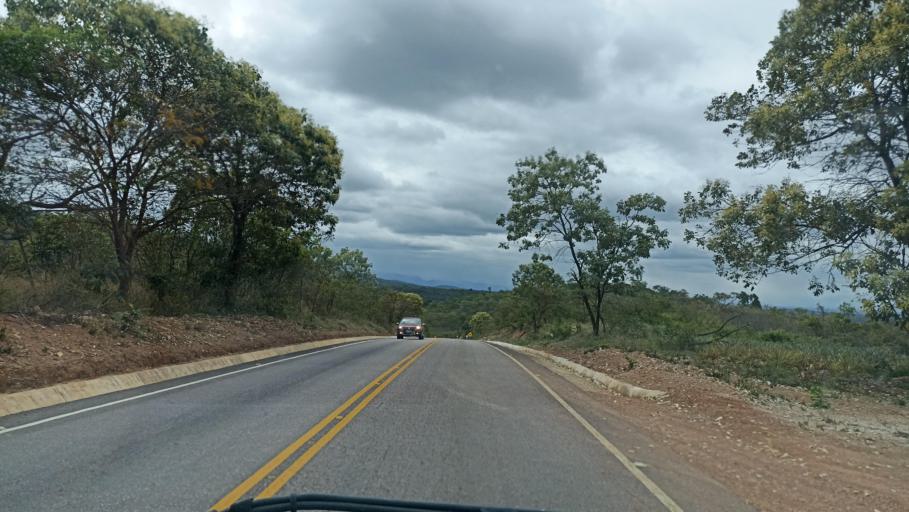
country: BR
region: Bahia
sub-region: Andarai
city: Vera Cruz
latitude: -12.9278
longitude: -41.2304
